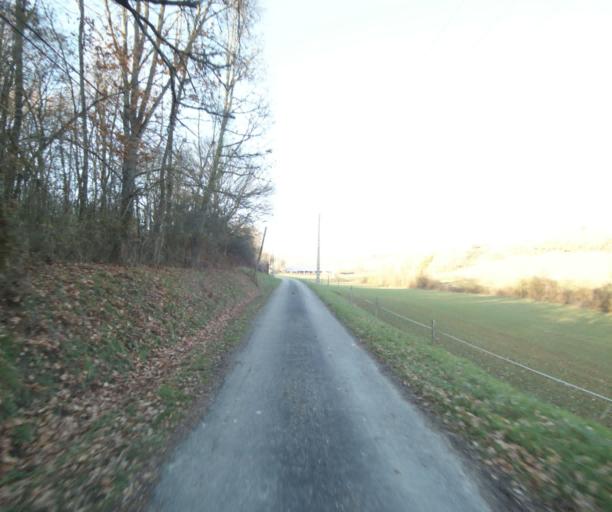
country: FR
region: Midi-Pyrenees
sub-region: Departement du Tarn-et-Garonne
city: Moissac
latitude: 44.1334
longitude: 1.1312
